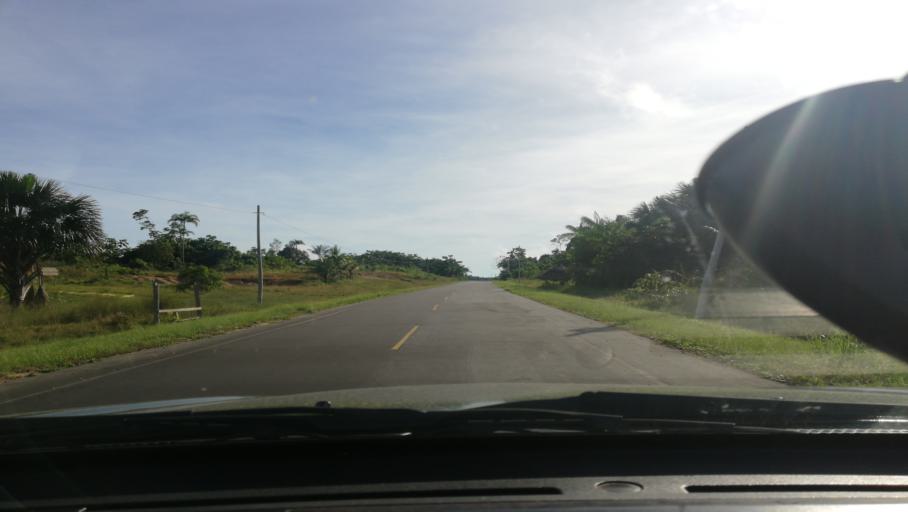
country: PE
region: Loreto
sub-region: Provincia de Loreto
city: Nauta
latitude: -4.3367
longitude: -73.5363
